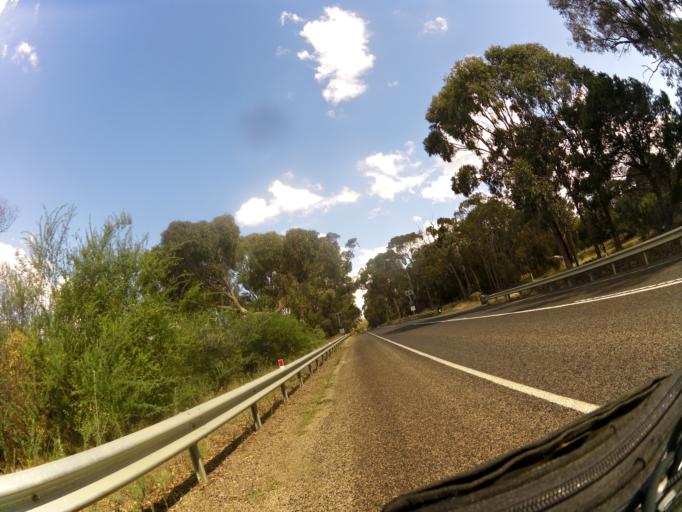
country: AU
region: Victoria
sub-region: Mansfield
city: Mansfield
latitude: -36.8334
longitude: 146.0080
